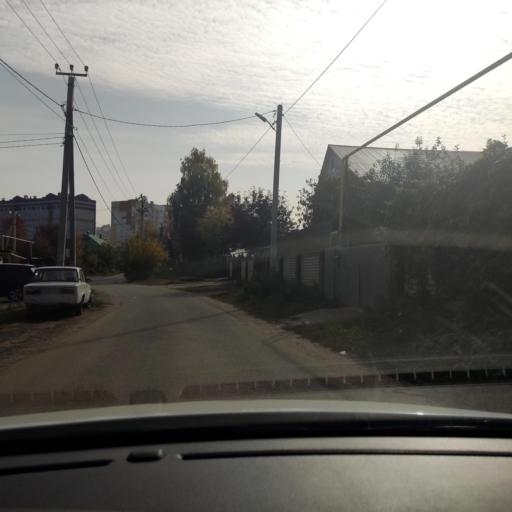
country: RU
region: Tatarstan
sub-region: Gorod Kazan'
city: Kazan
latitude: 55.8090
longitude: 49.2050
